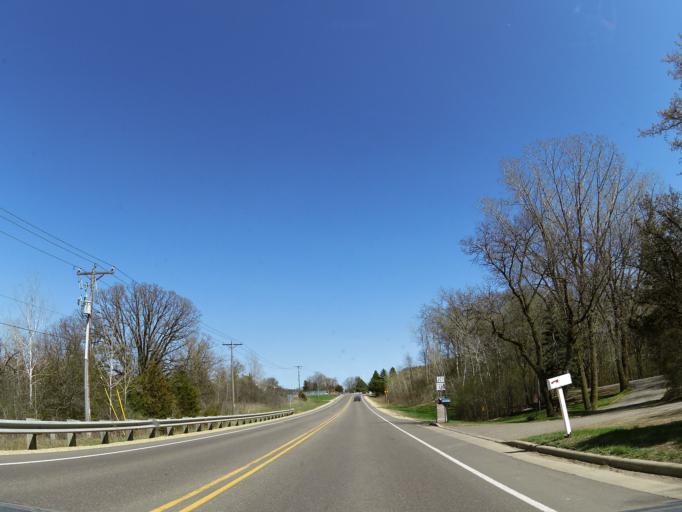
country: US
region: Wisconsin
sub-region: Saint Croix County
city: Hudson
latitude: 44.9596
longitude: -92.6846
